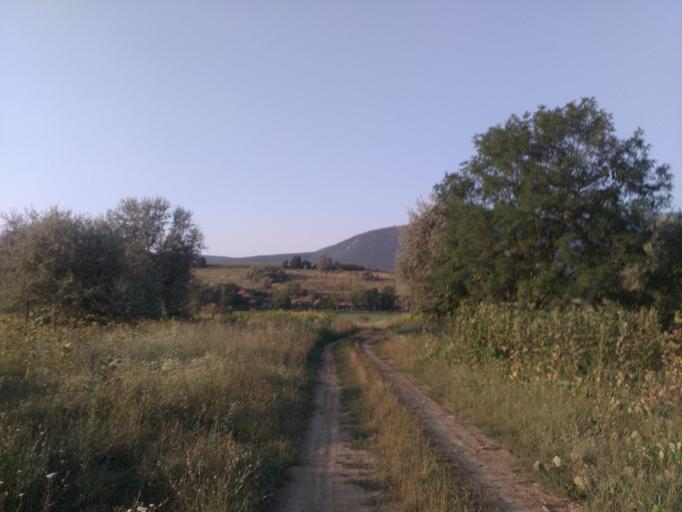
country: HU
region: Komarom-Esztergom
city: Piliscsev
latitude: 47.6712
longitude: 18.8241
